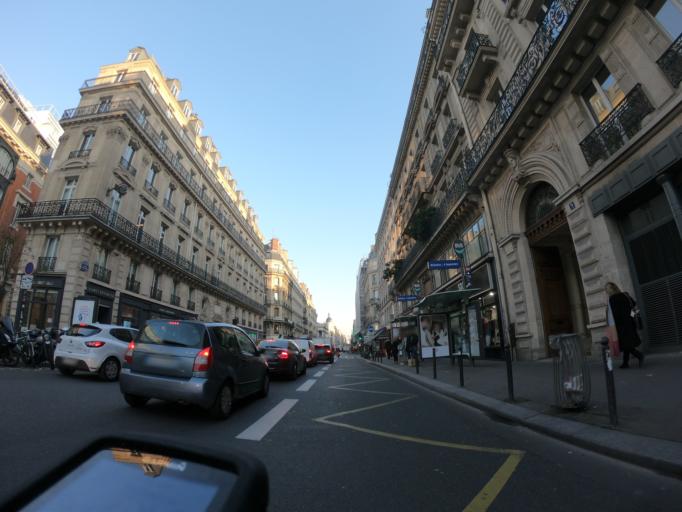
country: FR
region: Ile-de-France
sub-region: Paris
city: Paris
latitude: 48.8693
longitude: 2.3379
